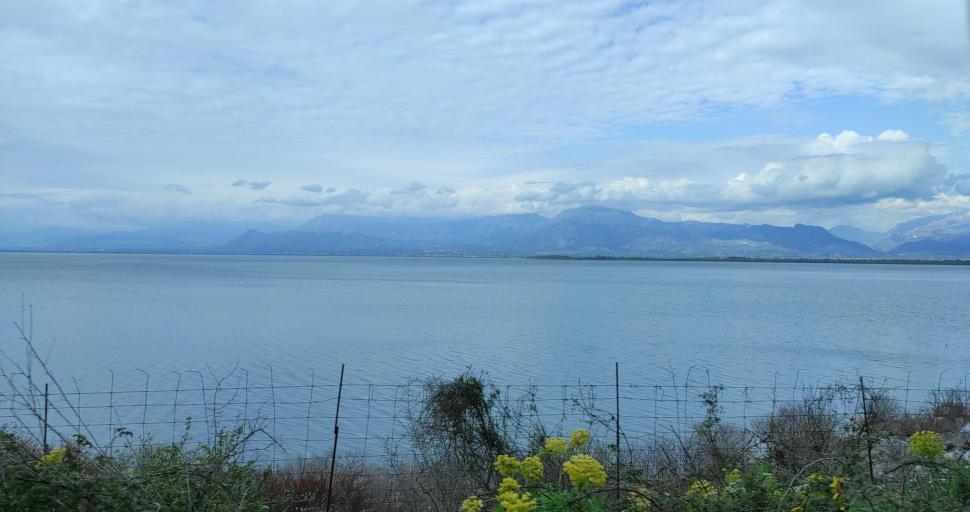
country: AL
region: Shkoder
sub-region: Rrethi i Shkodres
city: Berdica e Madhe
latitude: 42.0651
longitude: 19.4328
